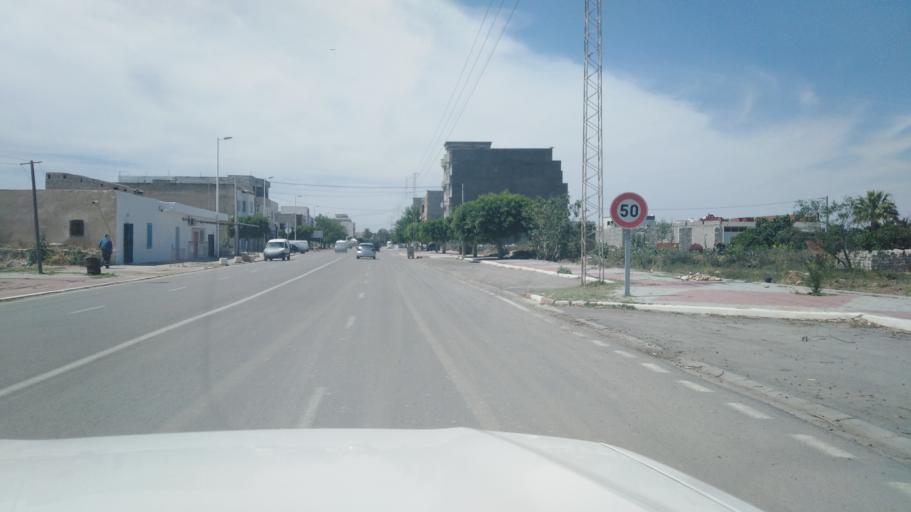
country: TN
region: Al Mahdiyah
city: Ksour Essaf
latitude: 35.4301
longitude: 11.0022
